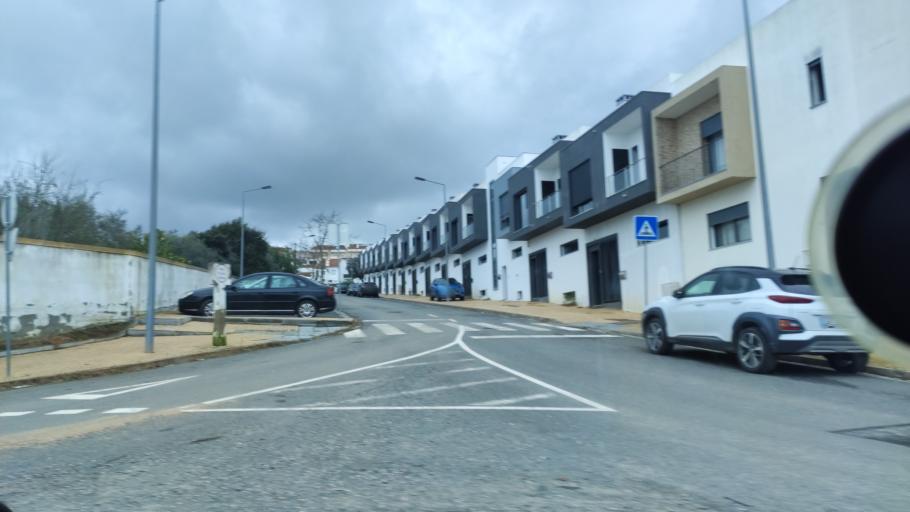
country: PT
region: Beja
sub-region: Beja
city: Beja
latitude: 38.0157
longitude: -7.8527
